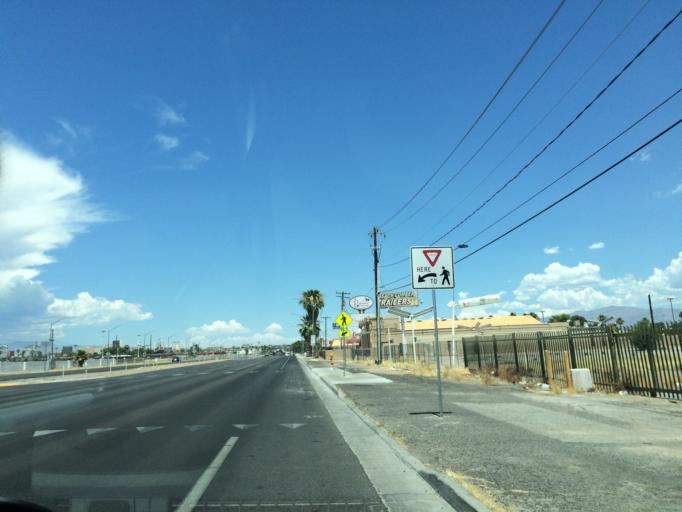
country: US
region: Nevada
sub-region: Clark County
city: Winchester
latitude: 36.1521
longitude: -115.1083
